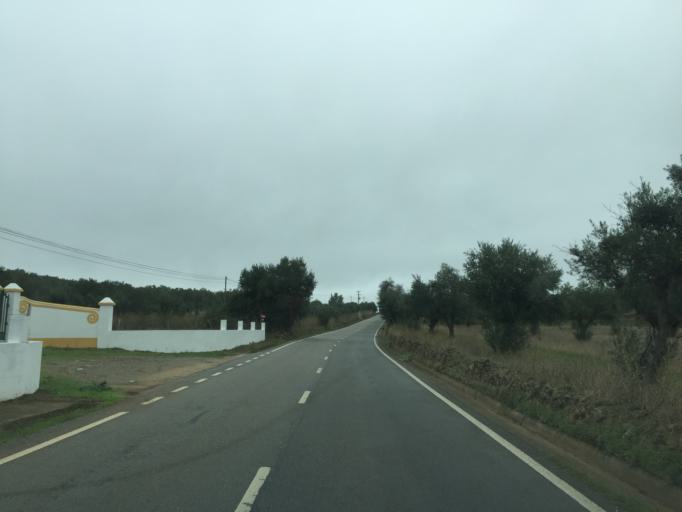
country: PT
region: Portalegre
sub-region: Alter do Chao
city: Alter do Chao
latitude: 39.2080
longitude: -7.6565
